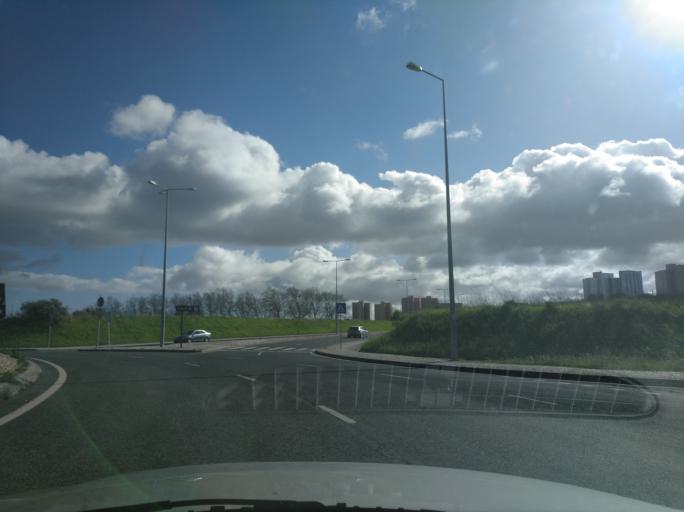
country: PT
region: Lisbon
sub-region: Loures
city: Loures
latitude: 38.8167
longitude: -9.1744
